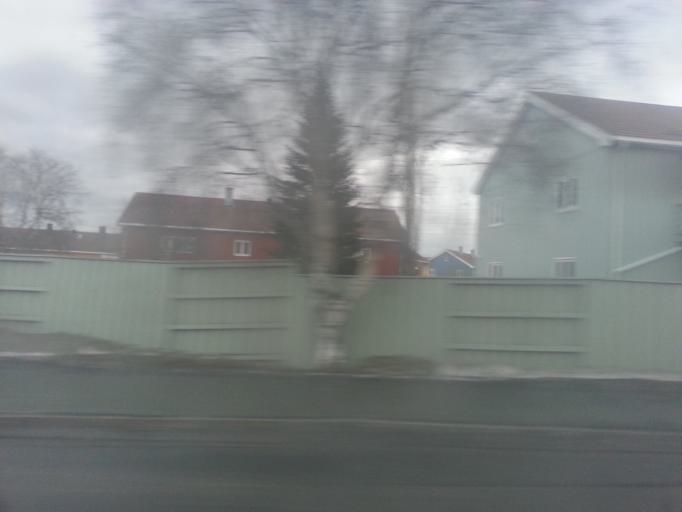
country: NO
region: Sor-Trondelag
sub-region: Trondheim
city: Trondheim
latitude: 63.4296
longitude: 10.4544
